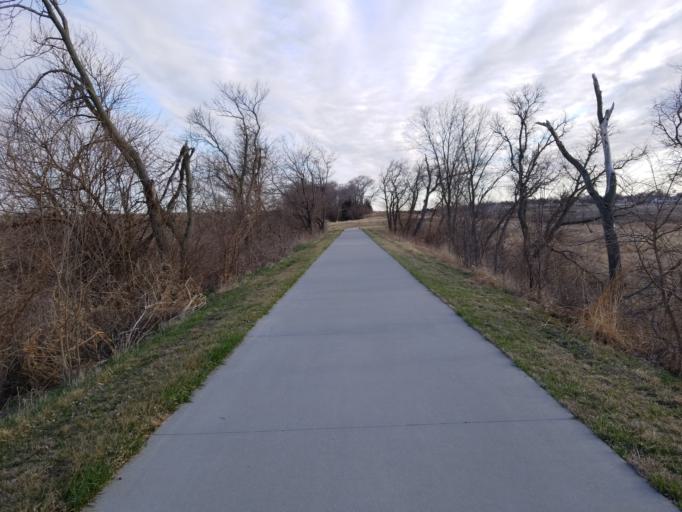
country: US
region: Nebraska
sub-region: Sarpy County
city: Chalco
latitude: 41.1518
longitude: -96.1137
